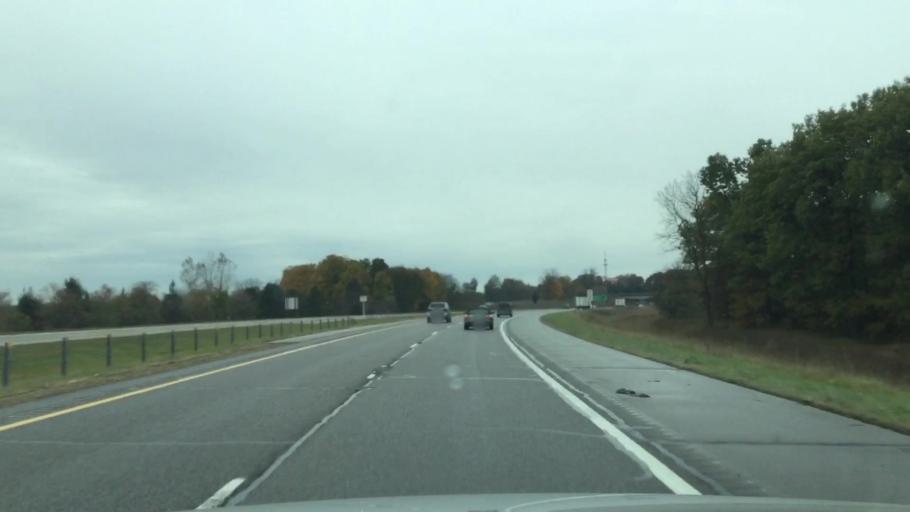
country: US
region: Michigan
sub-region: Calhoun County
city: Albion
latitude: 42.2651
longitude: -84.7696
